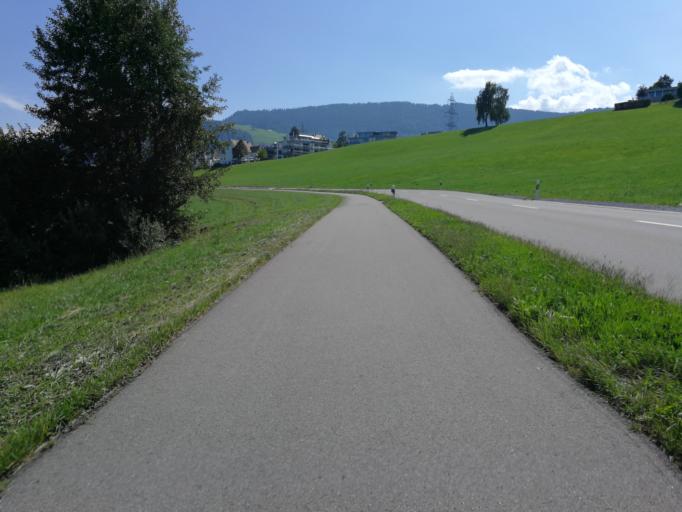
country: CH
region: Zurich
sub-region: Bezirk Horgen
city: Waedenswil / Eichweid
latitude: 47.1975
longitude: 8.6740
